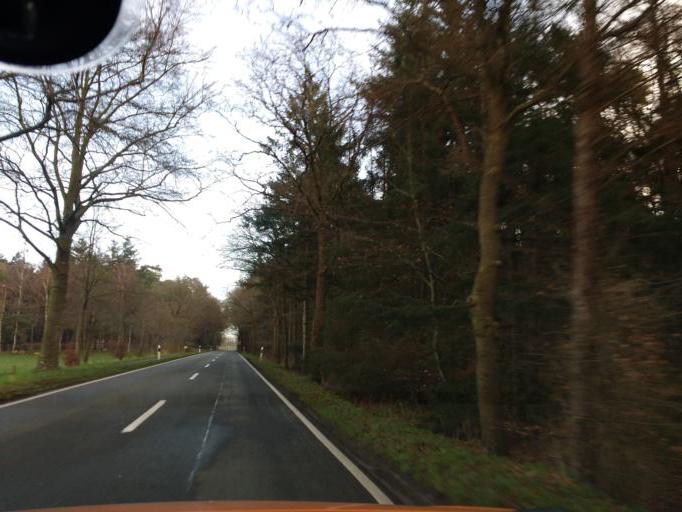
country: DE
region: Lower Saxony
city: Hude
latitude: 53.1211
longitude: 8.4243
